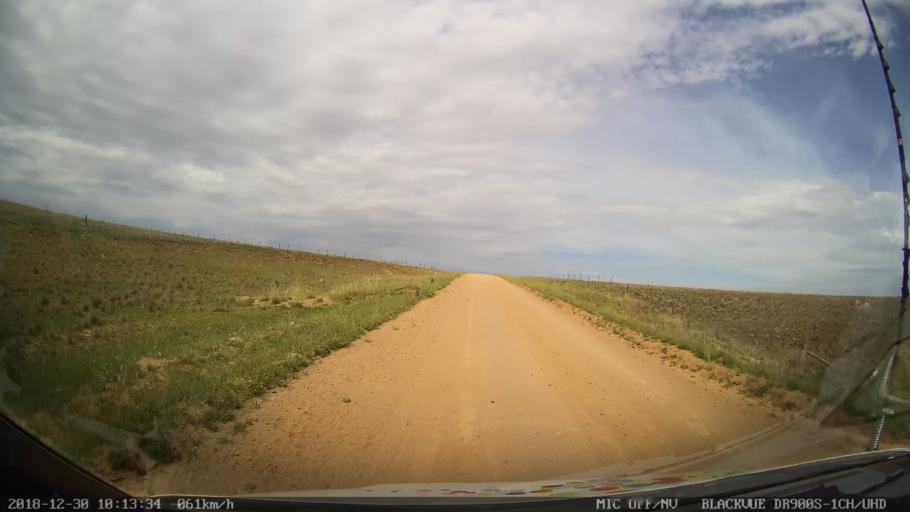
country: AU
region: New South Wales
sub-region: Snowy River
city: Berridale
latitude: -36.5383
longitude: 149.0636
